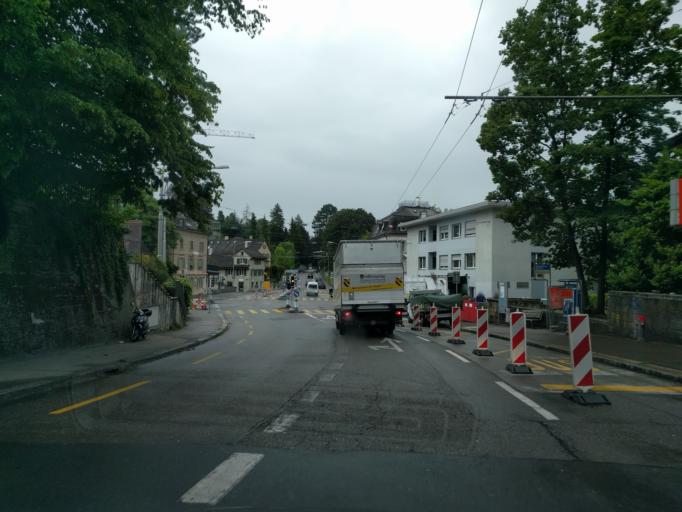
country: CH
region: Zurich
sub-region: Bezirk Zuerich
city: Zuerich (Kreis 8) / Muehlebach
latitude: 47.3600
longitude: 8.5573
